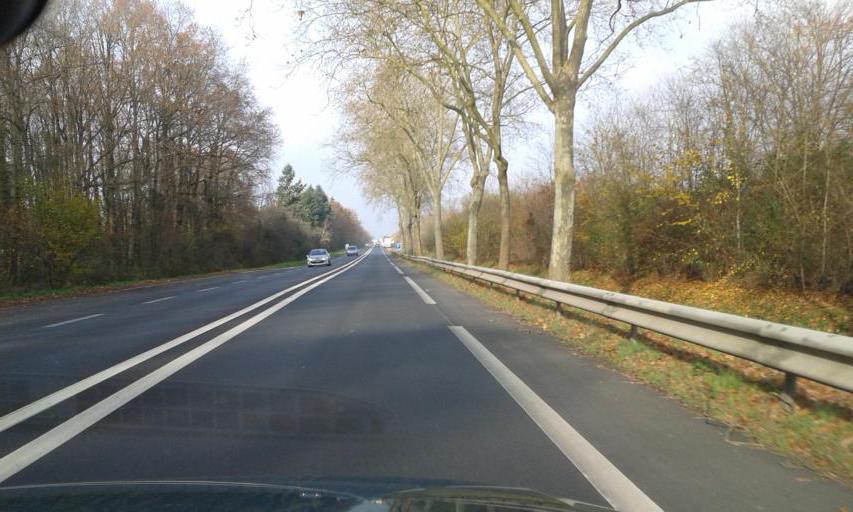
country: FR
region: Centre
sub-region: Departement du Loiret
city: Saint-Cyr-en-Val
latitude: 47.8172
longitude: 1.9266
